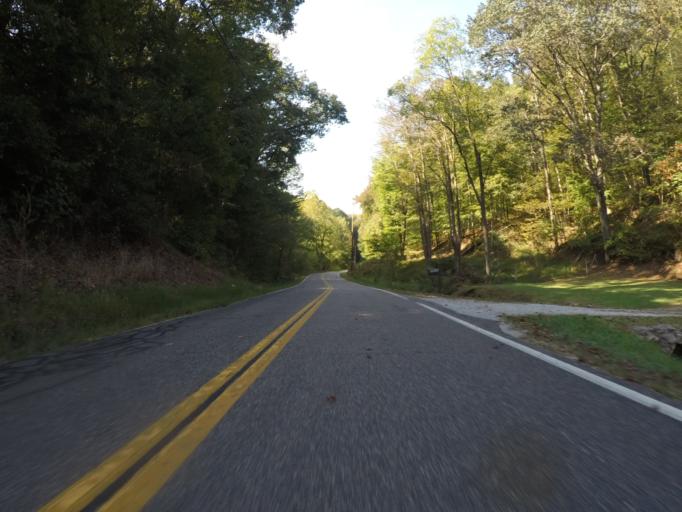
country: US
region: West Virginia
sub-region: Cabell County
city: Lesage
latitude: 38.6455
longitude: -82.4243
